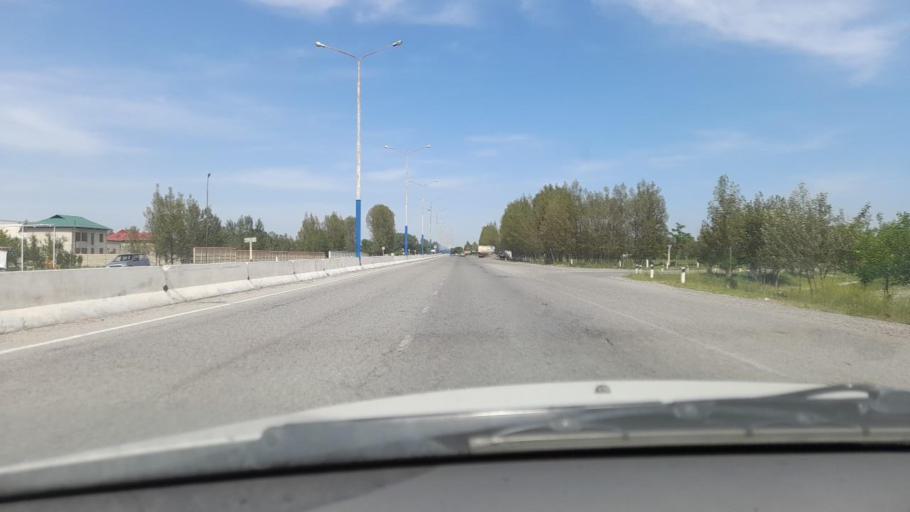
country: UZ
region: Samarqand
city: Ishtixon
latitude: 39.9374
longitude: 66.3829
